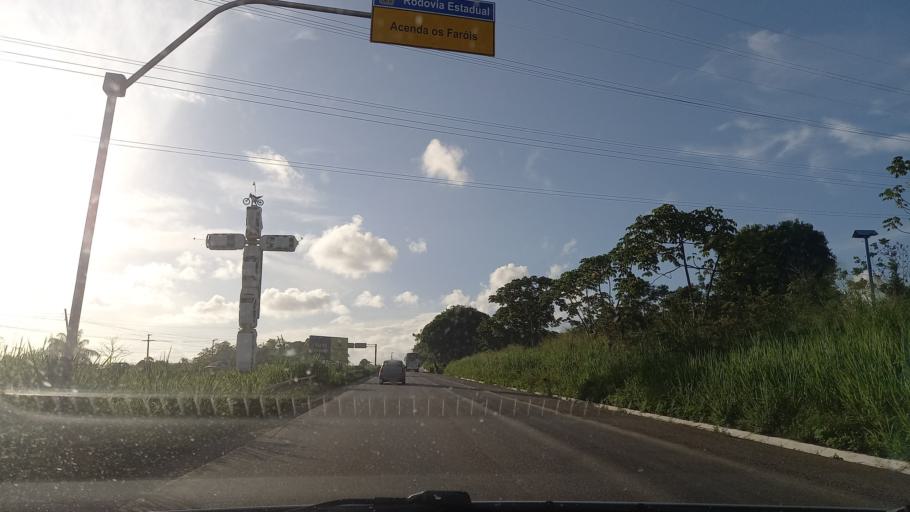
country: BR
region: Pernambuco
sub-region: Cabo De Santo Agostinho
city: Cabo
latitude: -8.3202
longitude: -35.0112
